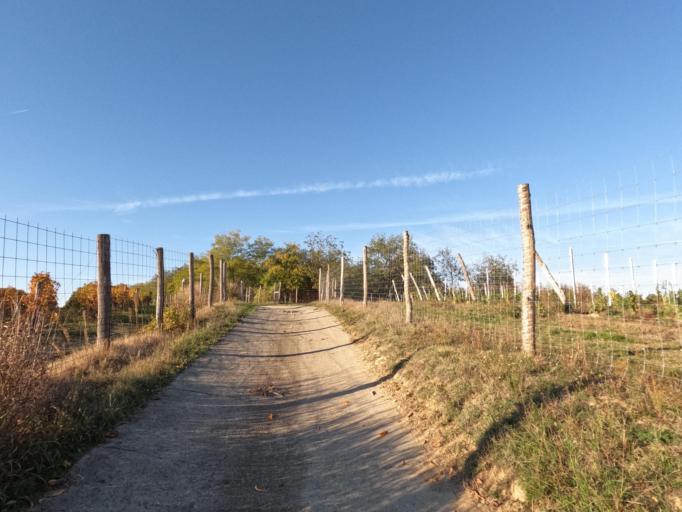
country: HU
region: Tolna
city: Szekszard
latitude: 46.3077
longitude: 18.6599
